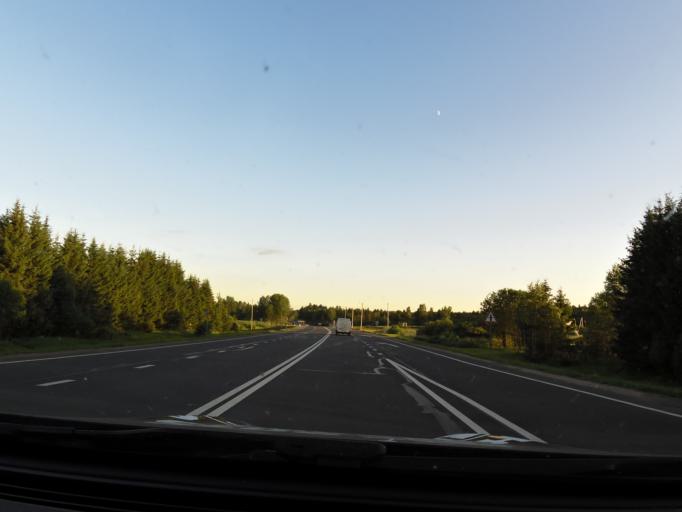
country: RU
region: Jaroslavl
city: Prechistoye
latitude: 58.4857
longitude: 40.3260
